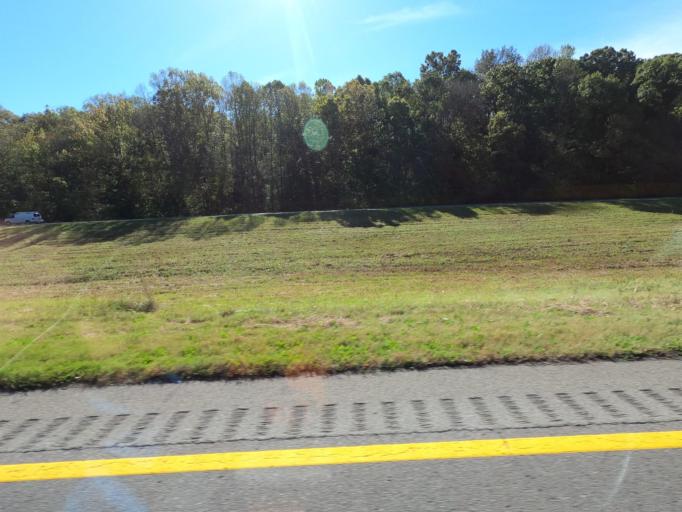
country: US
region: Tennessee
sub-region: Dickson County
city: White Bluff
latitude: 36.0255
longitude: -87.2208
